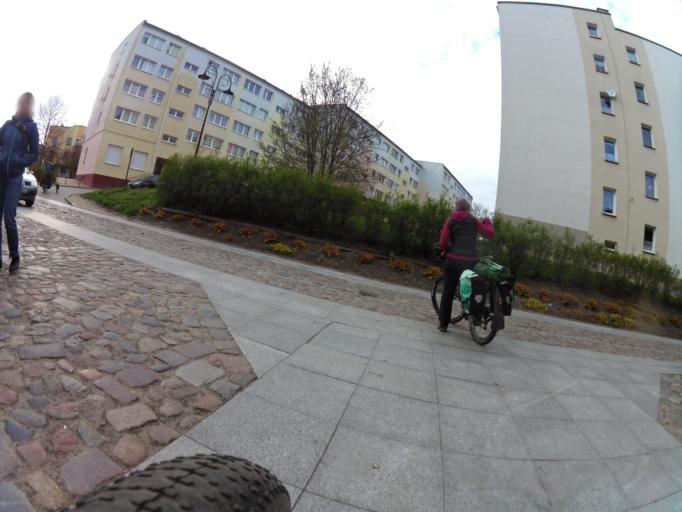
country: PL
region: West Pomeranian Voivodeship
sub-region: Powiat slawienski
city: Slawno
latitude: 54.3614
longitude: 16.6801
